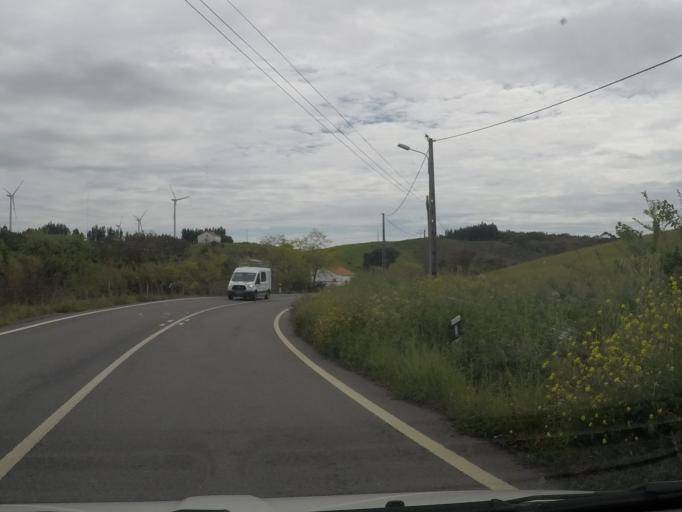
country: PT
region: Setubal
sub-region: Sines
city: Porto Covo
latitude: 37.8672
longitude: -8.7266
